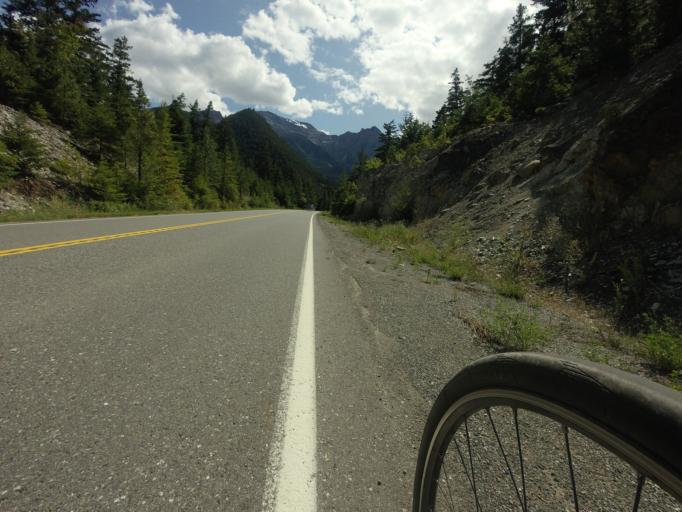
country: CA
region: British Columbia
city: Lillooet
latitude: 50.6609
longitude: -121.9919
